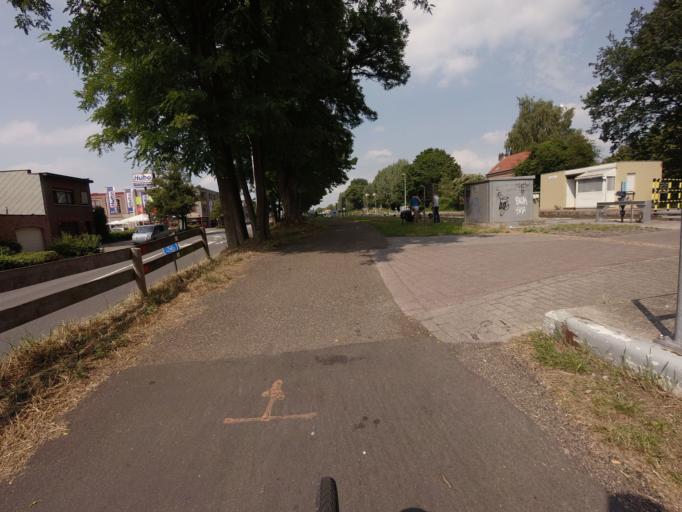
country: BE
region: Flanders
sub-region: Provincie Antwerpen
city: Schoten
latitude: 51.2500
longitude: 4.5059
